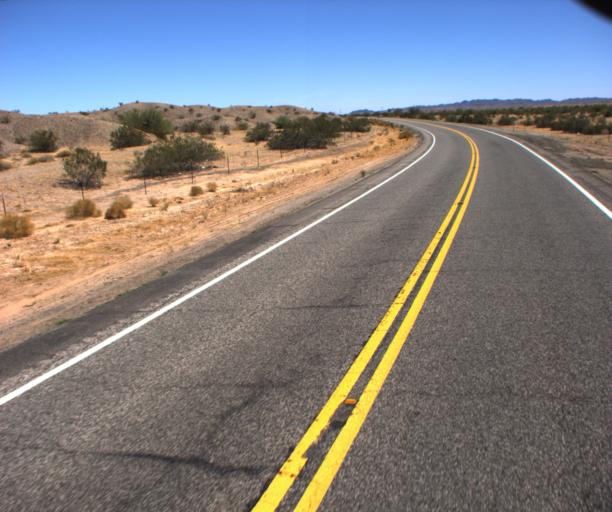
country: US
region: Arizona
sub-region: La Paz County
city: Parker
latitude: 33.9985
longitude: -114.2280
